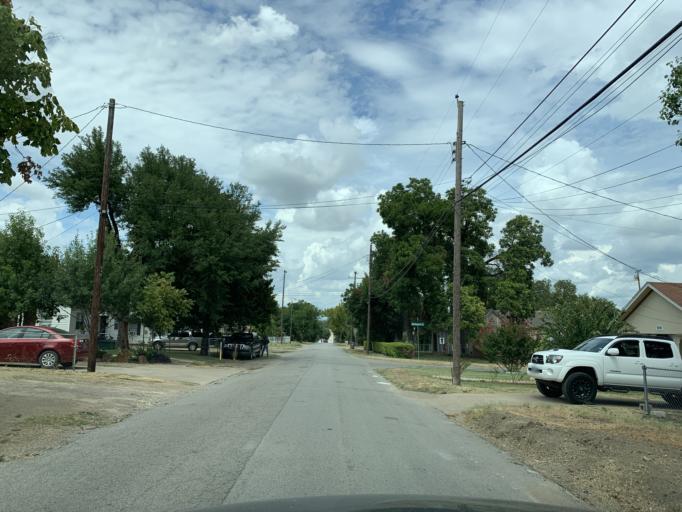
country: US
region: Texas
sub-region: Dallas County
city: Cockrell Hill
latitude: 32.7365
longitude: -96.8797
